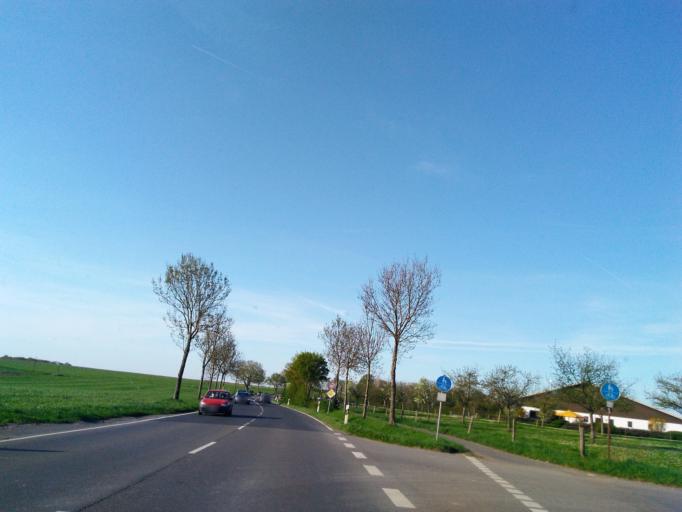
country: DE
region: North Rhine-Westphalia
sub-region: Regierungsbezirk Koln
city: Hennef
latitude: 50.8388
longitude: 7.2877
